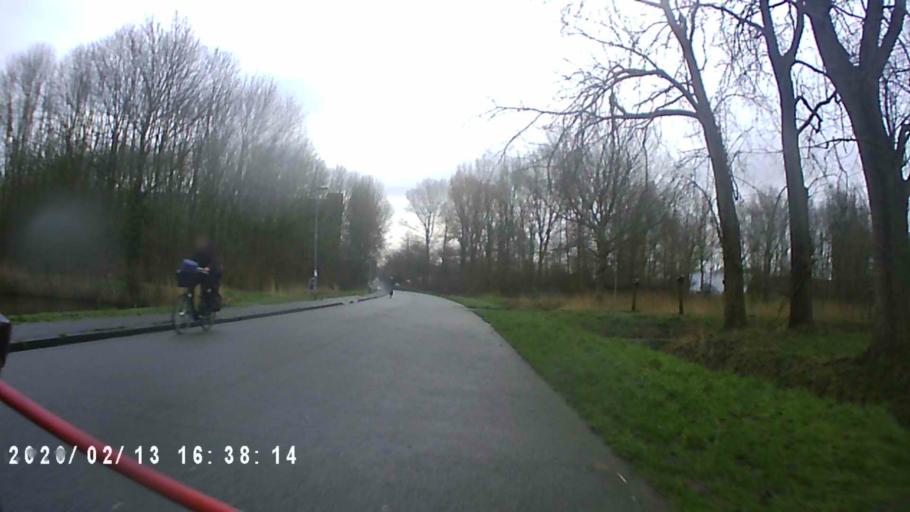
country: NL
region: Groningen
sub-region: Gemeente Groningen
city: Groningen
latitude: 53.2286
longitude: 6.5188
